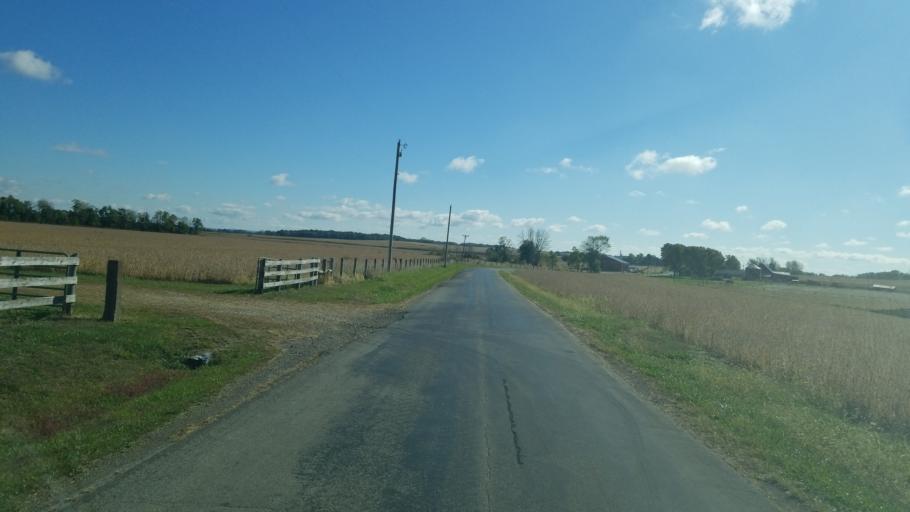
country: US
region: Ohio
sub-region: Highland County
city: Leesburg
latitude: 39.2814
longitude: -83.5757
